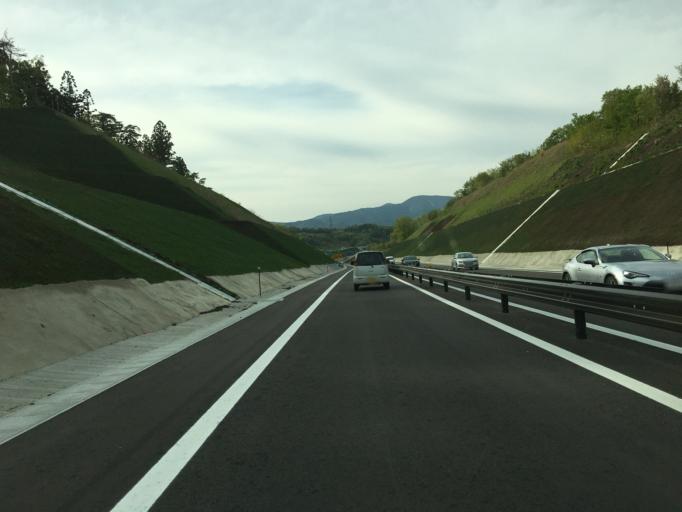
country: JP
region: Fukushima
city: Hobaramachi
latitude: 37.7940
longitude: 140.5497
